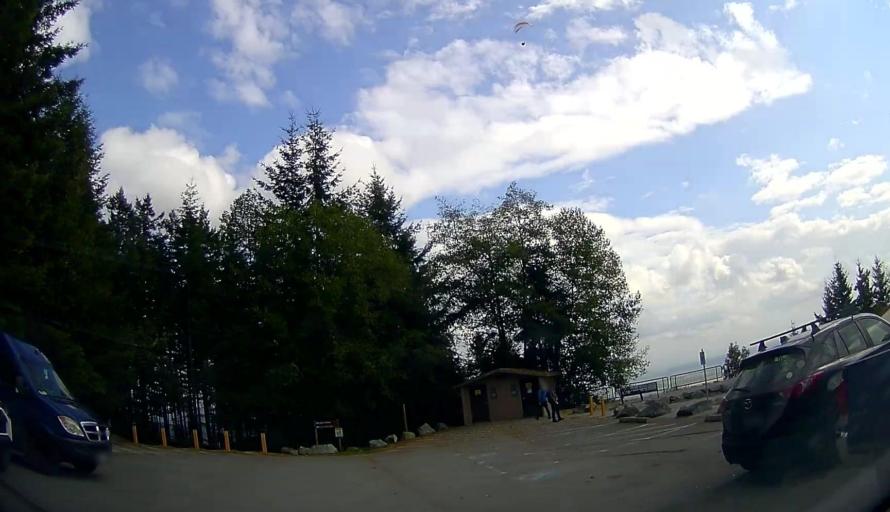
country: US
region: Washington
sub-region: Whatcom County
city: Geneva
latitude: 48.6100
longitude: -122.4263
